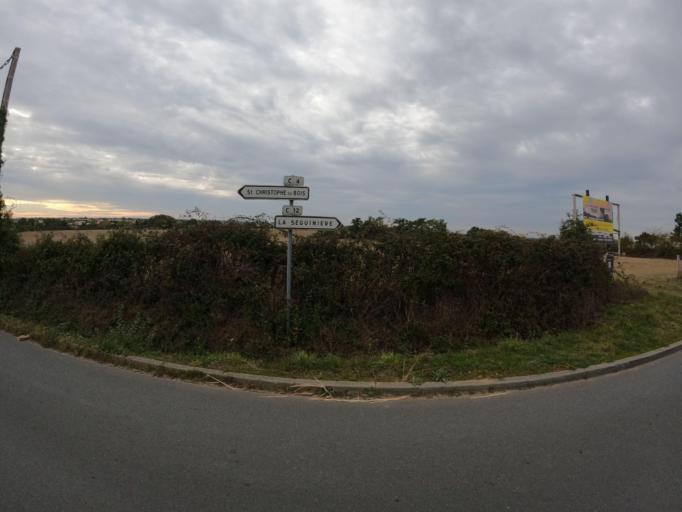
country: FR
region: Pays de la Loire
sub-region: Departement de Maine-et-Loire
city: Saint-Christophe-du-Bois
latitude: 47.0376
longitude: -0.9362
